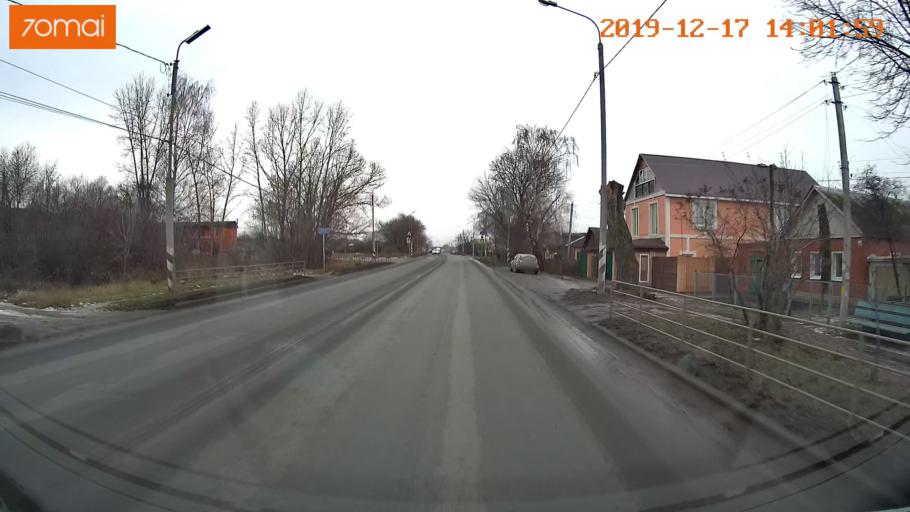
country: RU
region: Rjazan
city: Ryazan'
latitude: 54.6168
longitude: 39.6518
